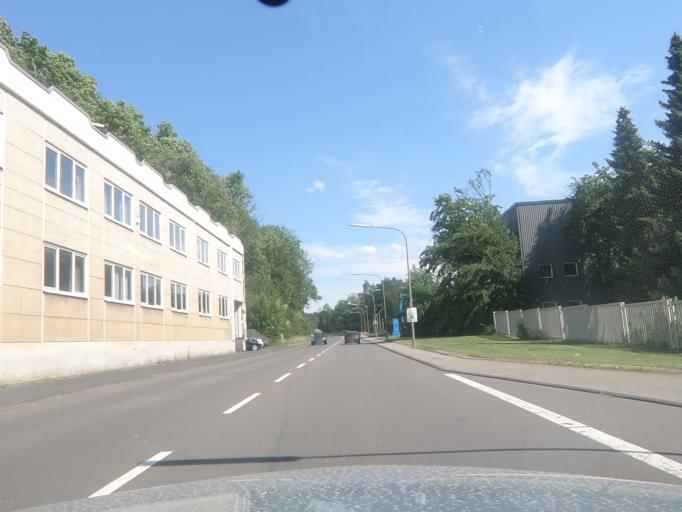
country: DE
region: North Rhine-Westphalia
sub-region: Regierungsbezirk Arnsberg
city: Finnentrop
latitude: 51.1689
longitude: 7.9699
